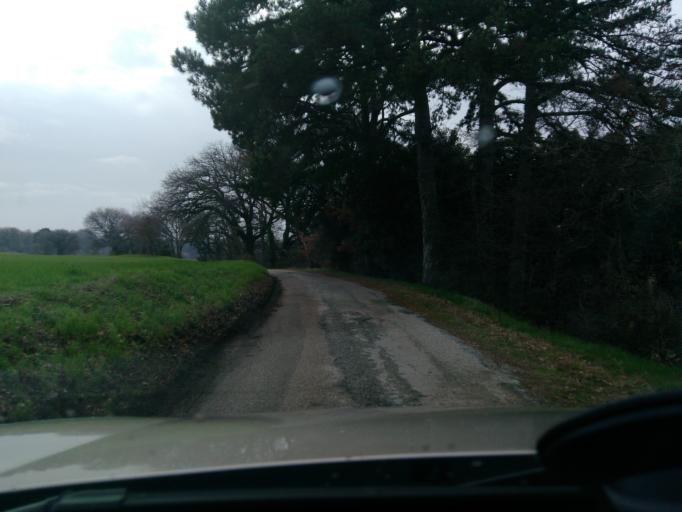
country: FR
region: Rhone-Alpes
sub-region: Departement de la Drome
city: Savasse
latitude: 44.5756
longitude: 4.7726
